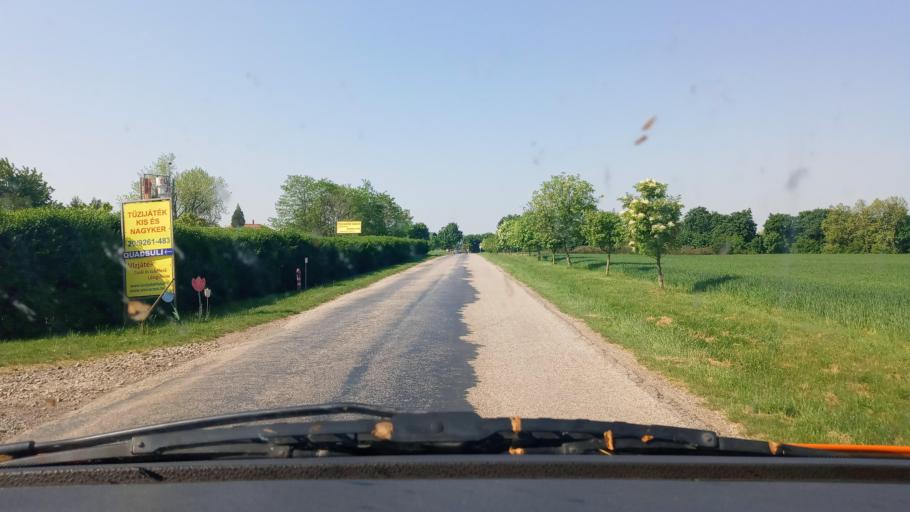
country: HU
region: Baranya
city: Kozarmisleny
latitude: 45.9962
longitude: 18.3147
